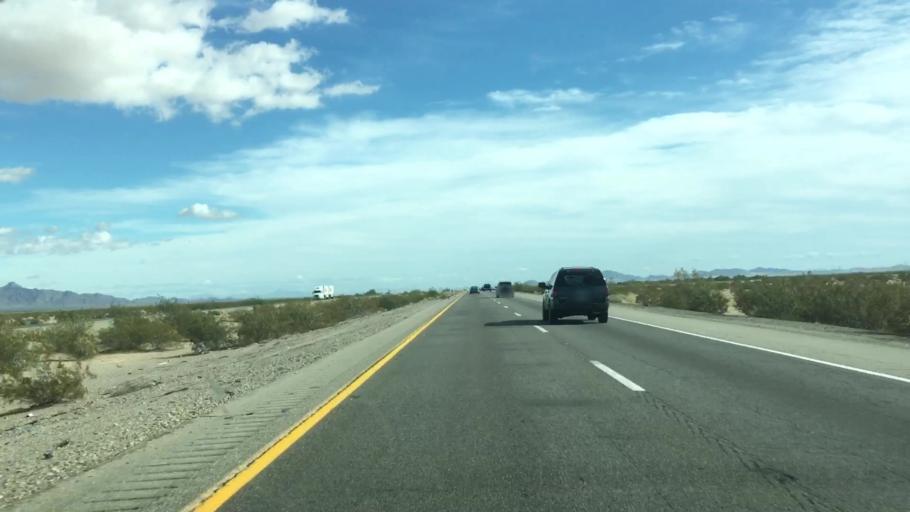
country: US
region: California
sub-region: Riverside County
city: Mesa Verde
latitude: 33.6227
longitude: -115.0432
